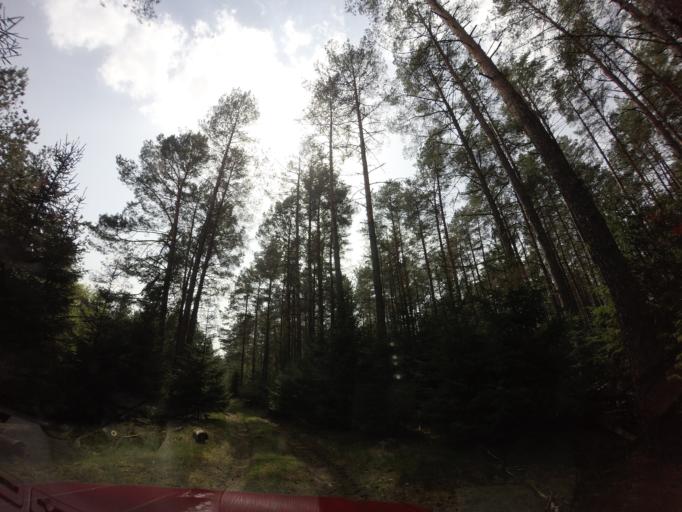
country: PL
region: West Pomeranian Voivodeship
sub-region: Powiat choszczenski
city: Drawno
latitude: 53.2766
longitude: 15.7159
